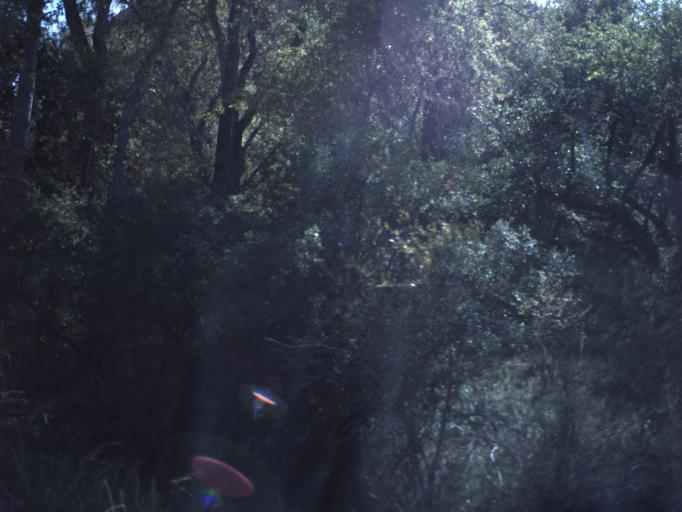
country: US
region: Utah
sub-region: San Juan County
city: Monticello
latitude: 38.0169
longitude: -109.5393
